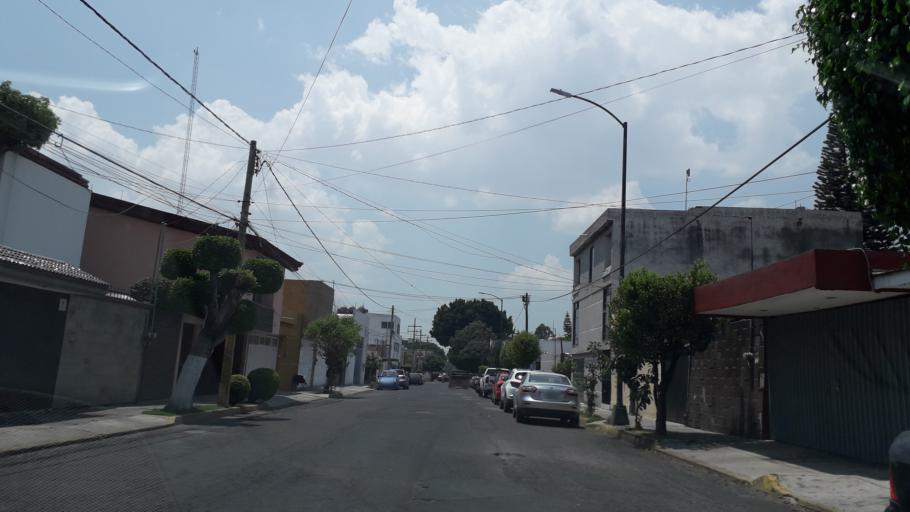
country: MX
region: Puebla
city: Puebla
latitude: 19.0291
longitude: -98.2175
